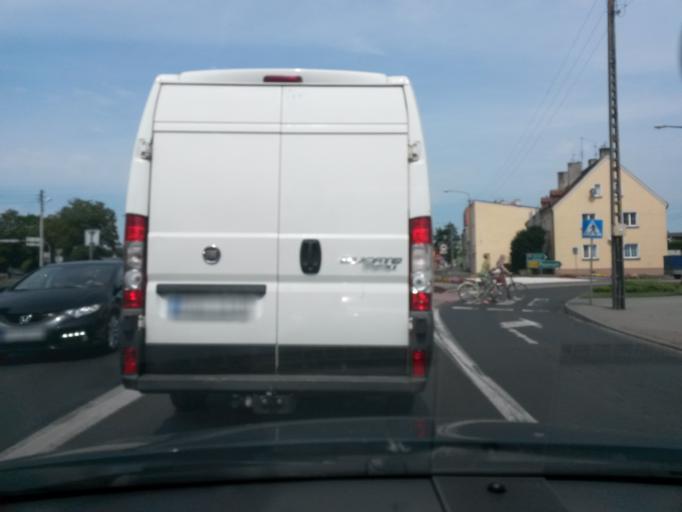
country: PL
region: Greater Poland Voivodeship
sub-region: Powiat gostynski
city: Gostyn
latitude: 51.8768
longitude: 17.0117
